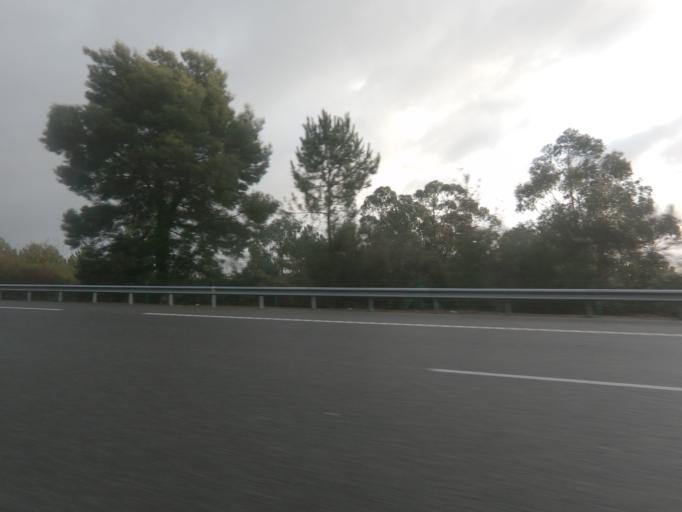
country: ES
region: Galicia
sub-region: Provincia de Pontevedra
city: Porrino
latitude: 42.1786
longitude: -8.6502
